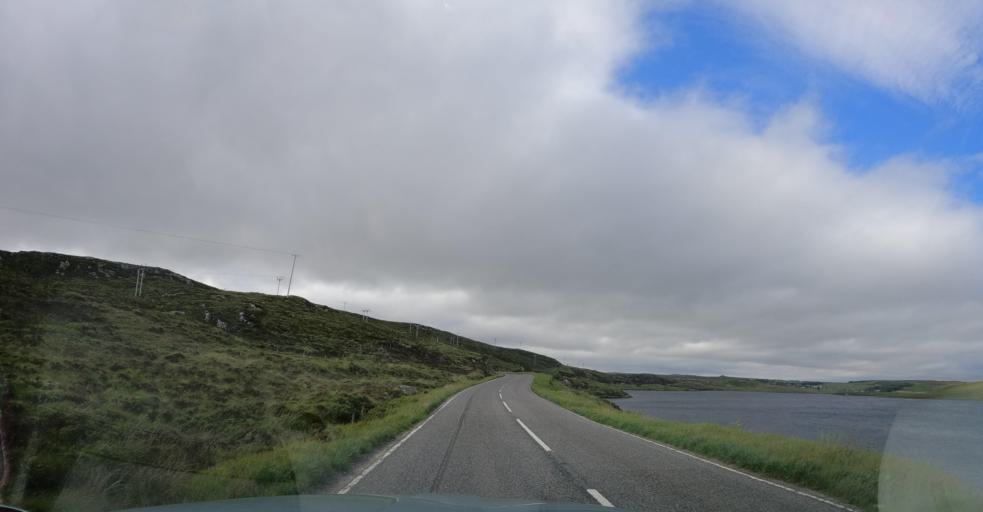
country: GB
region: Scotland
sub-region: Eilean Siar
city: Stornoway
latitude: 58.1346
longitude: -6.5079
